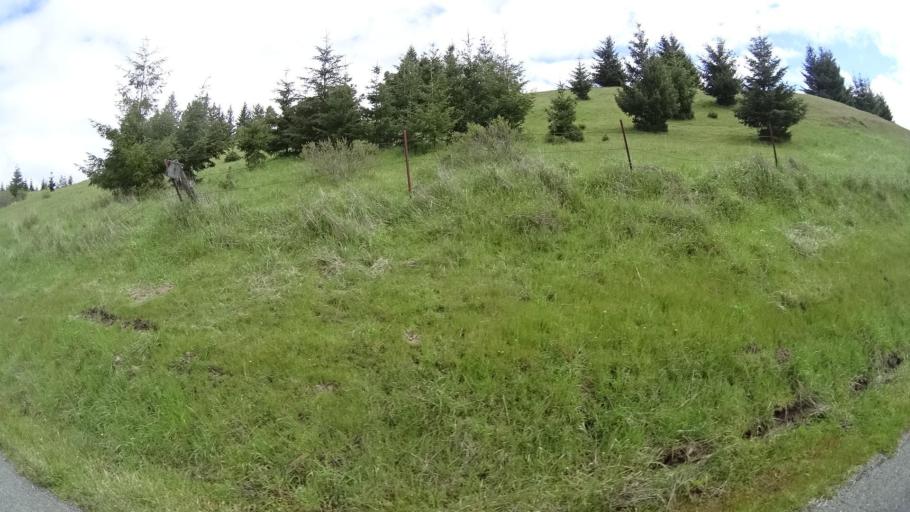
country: US
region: California
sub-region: Humboldt County
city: Blue Lake
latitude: 40.7895
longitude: -123.9673
